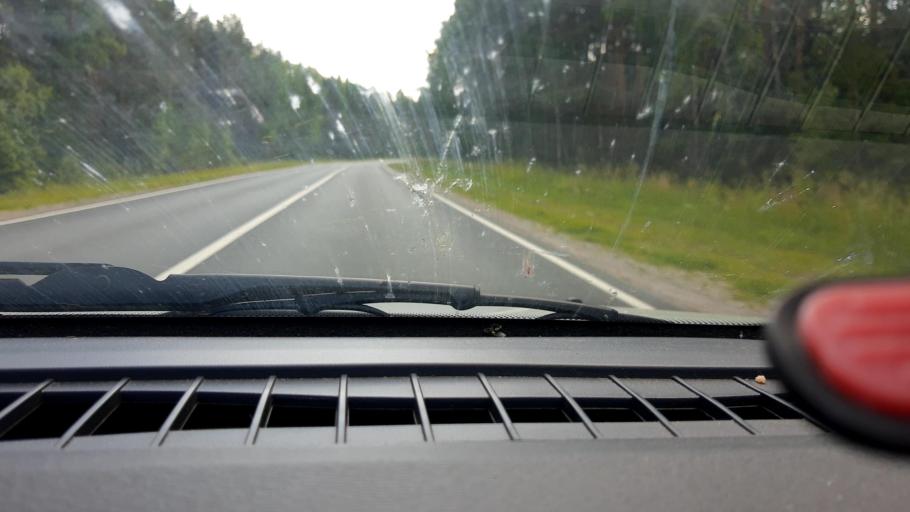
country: RU
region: Nizjnij Novgorod
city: Krasnyye Baki
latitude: 57.2187
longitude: 45.4842
